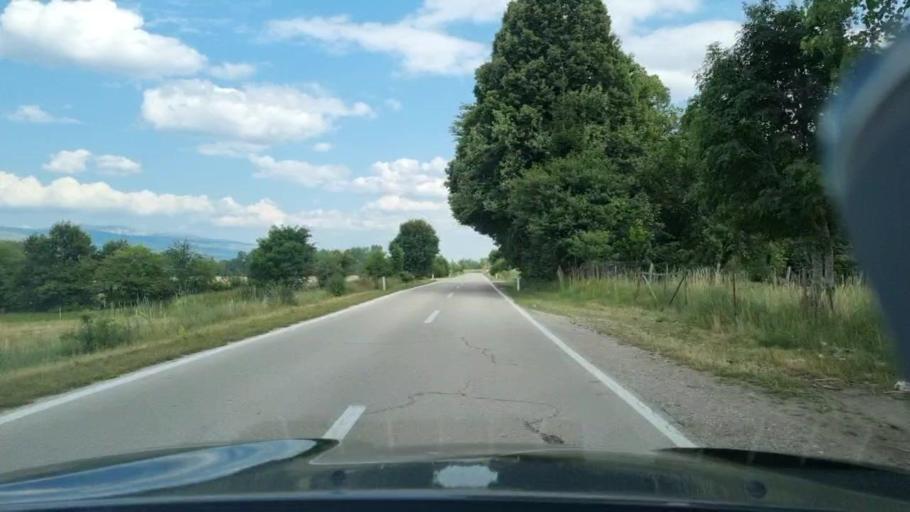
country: BA
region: Federation of Bosnia and Herzegovina
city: Glamoc
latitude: 43.9839
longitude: 16.6365
